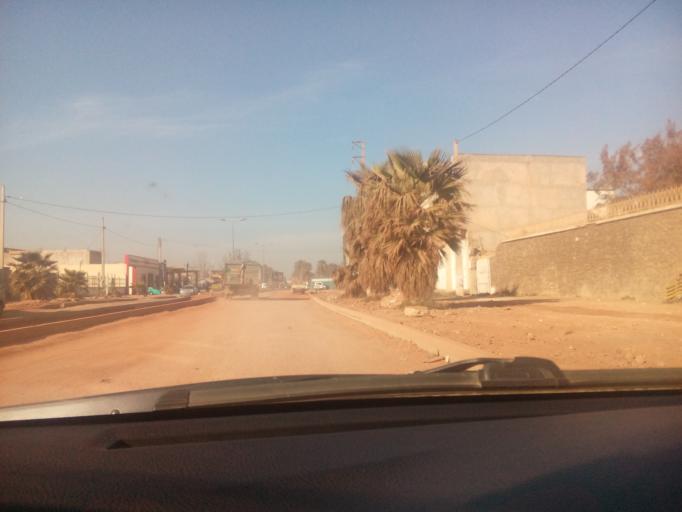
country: DZ
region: Oran
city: Es Senia
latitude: 35.6473
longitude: -0.6107
